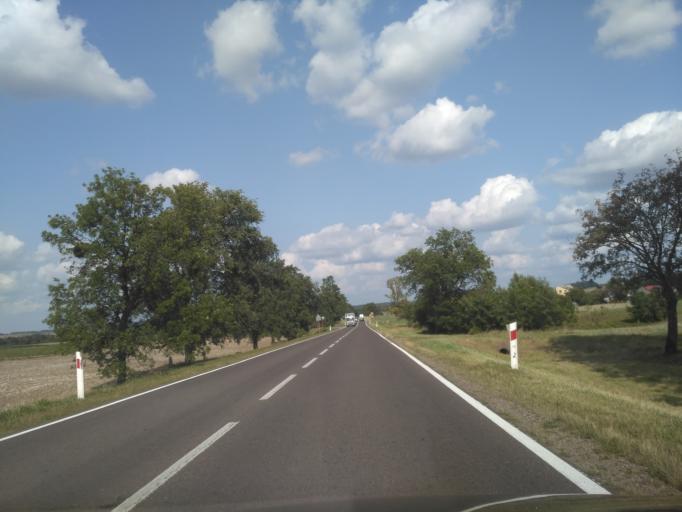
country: PL
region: Lublin Voivodeship
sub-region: Powiat chelmski
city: Rejowiec
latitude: 51.1101
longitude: 23.3170
